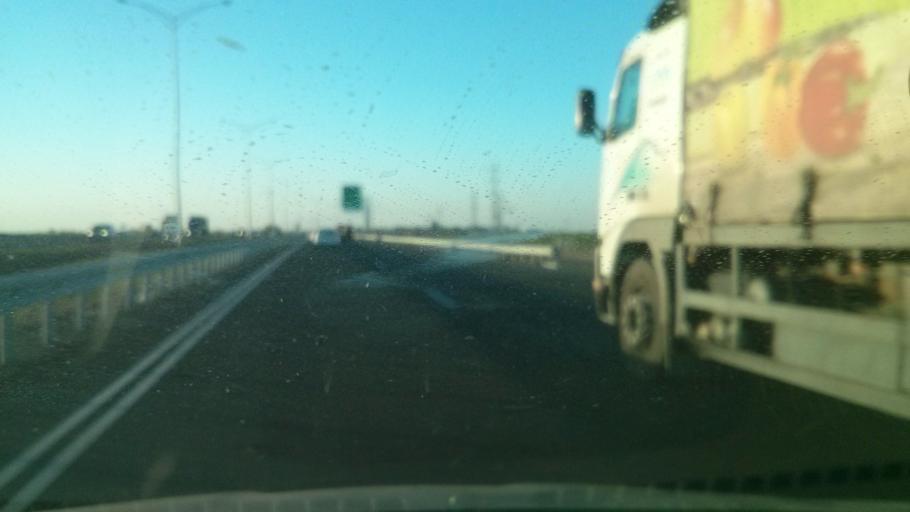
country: IL
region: Southern District
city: Lehavim
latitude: 31.4311
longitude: 34.7783
